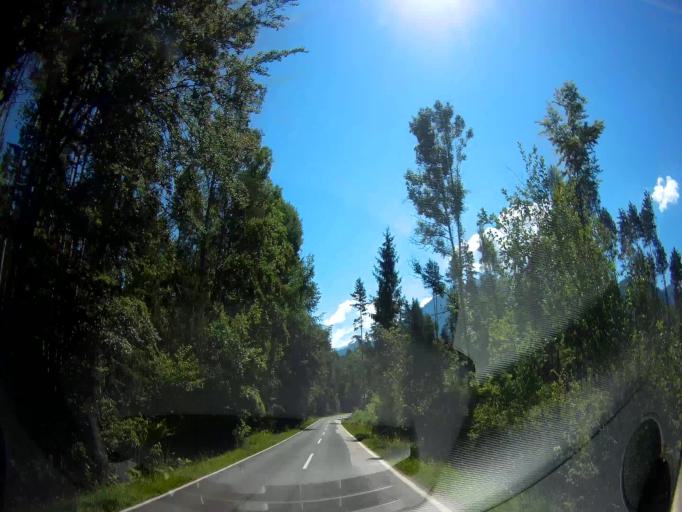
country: AT
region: Carinthia
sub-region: Politischer Bezirk Volkermarkt
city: Sittersdorf
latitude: 46.5380
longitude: 14.5753
